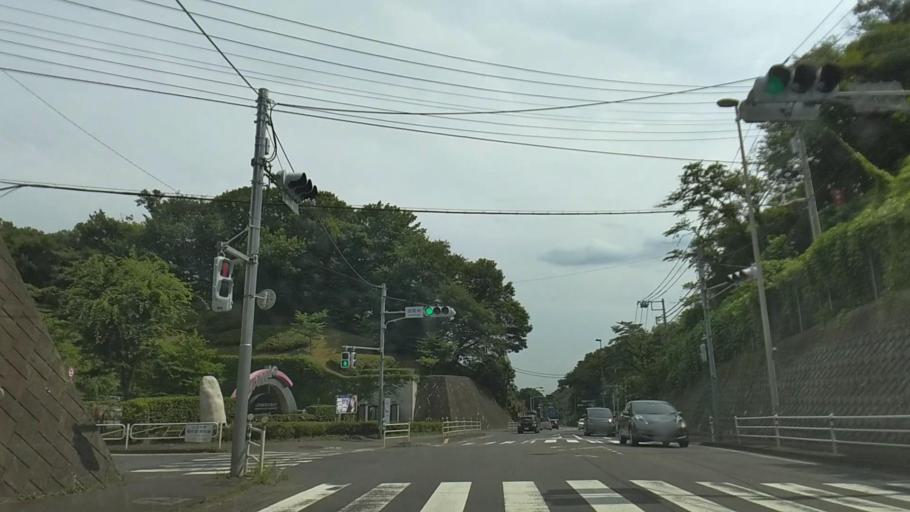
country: JP
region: Tokyo
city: Hachioji
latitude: 35.6214
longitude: 139.3411
